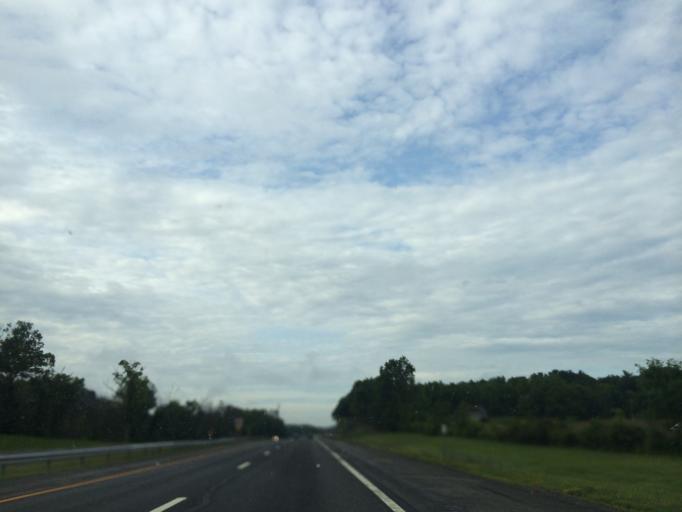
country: US
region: New York
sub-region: Ulster County
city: Saugerties
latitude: 42.1187
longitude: -73.9562
